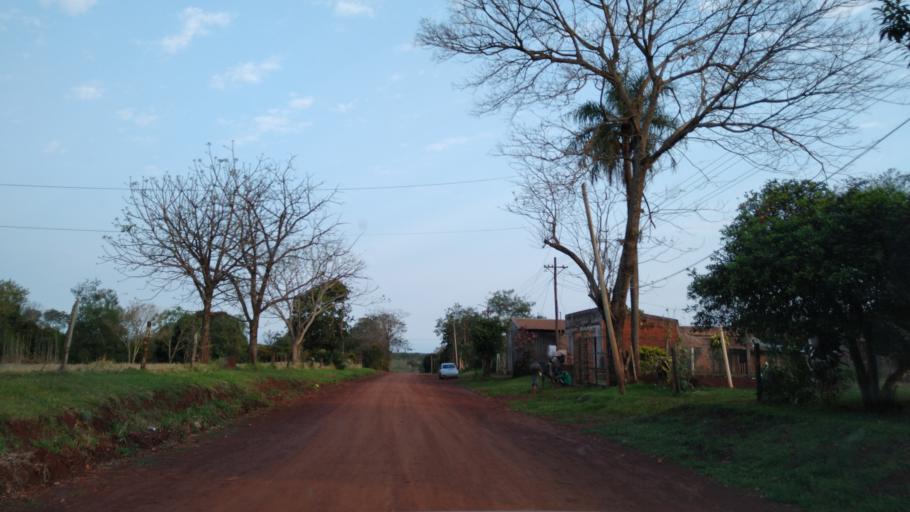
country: AR
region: Corrientes
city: San Carlos
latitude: -27.7486
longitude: -55.9009
